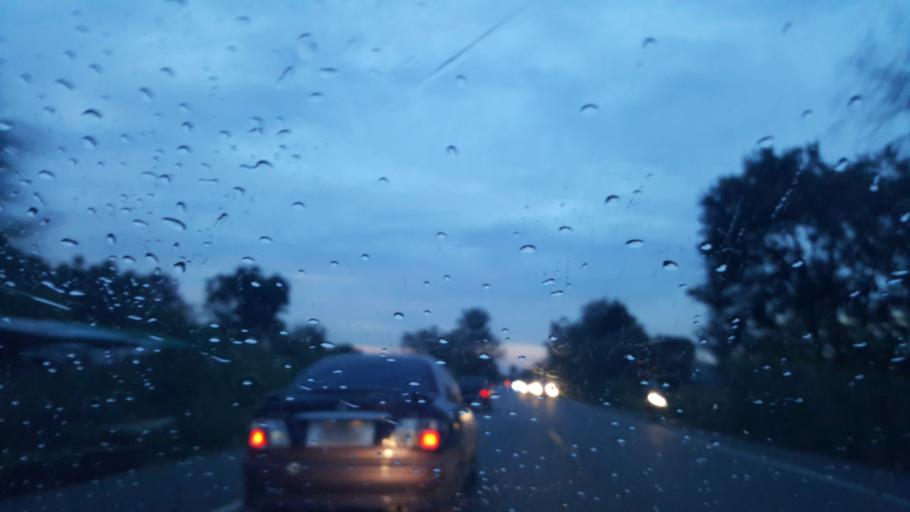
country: TH
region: Chon Buri
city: Sattahip
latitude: 12.7311
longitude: 100.9546
